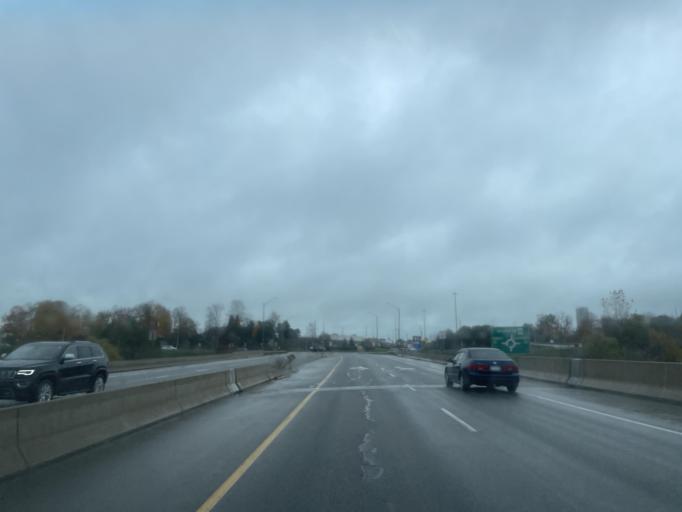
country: CA
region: Ontario
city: Cambridge
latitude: 43.4215
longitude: -80.3301
